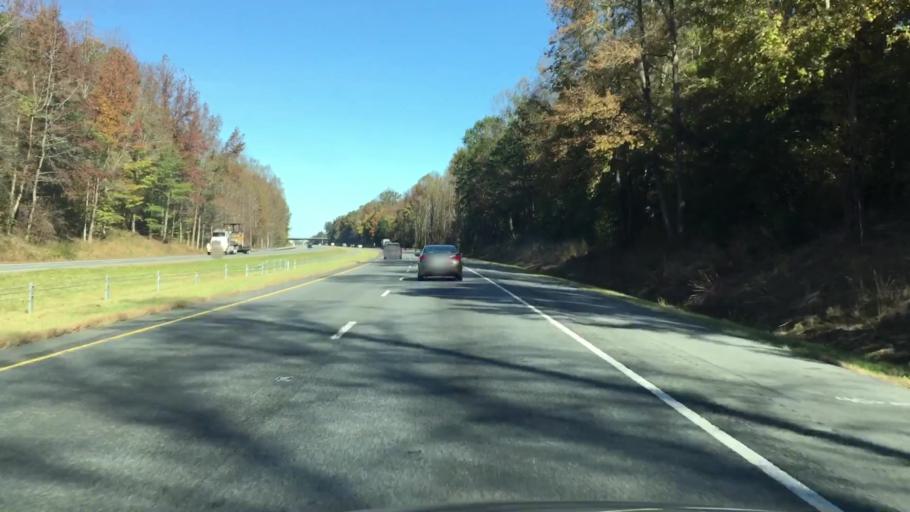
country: US
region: North Carolina
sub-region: Rockingham County
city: Reidsville
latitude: 36.2782
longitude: -79.6400
